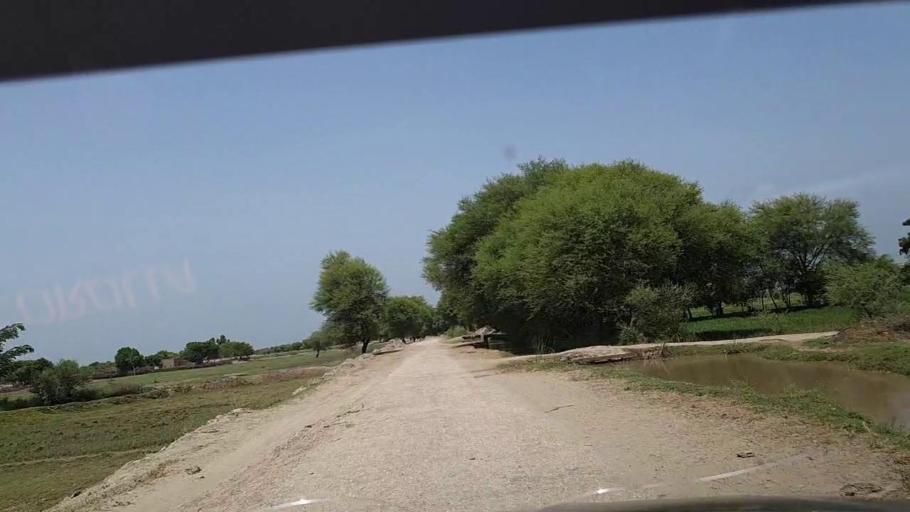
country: PK
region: Sindh
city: Khanpur
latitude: 27.8110
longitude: 69.4505
